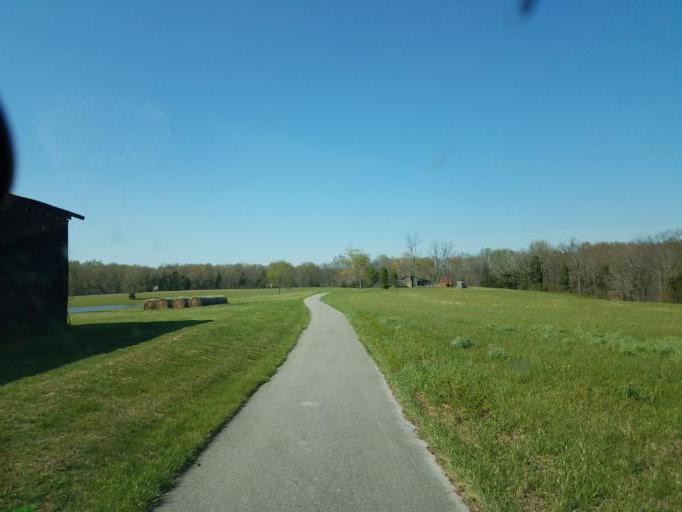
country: US
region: Kentucky
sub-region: Edmonson County
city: Brownsville
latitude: 37.1352
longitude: -86.1471
